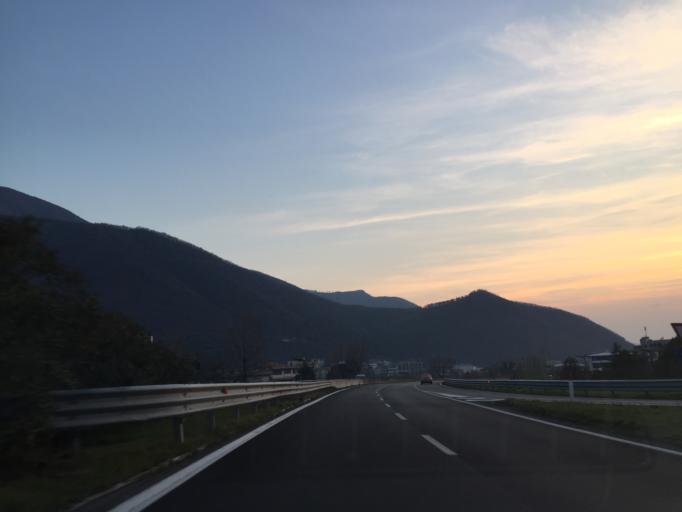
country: IT
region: Campania
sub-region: Provincia di Avellino
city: Solofra
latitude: 40.8363
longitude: 14.8402
